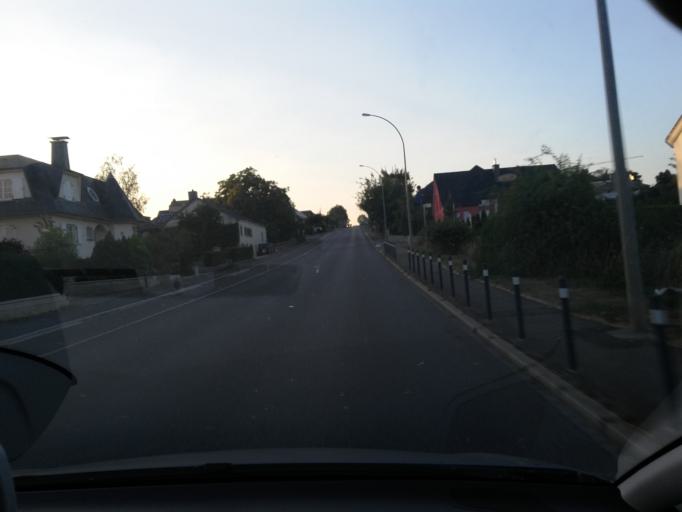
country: LU
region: Luxembourg
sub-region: Canton d'Esch-sur-Alzette
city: Frisange
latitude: 49.5204
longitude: 6.1865
